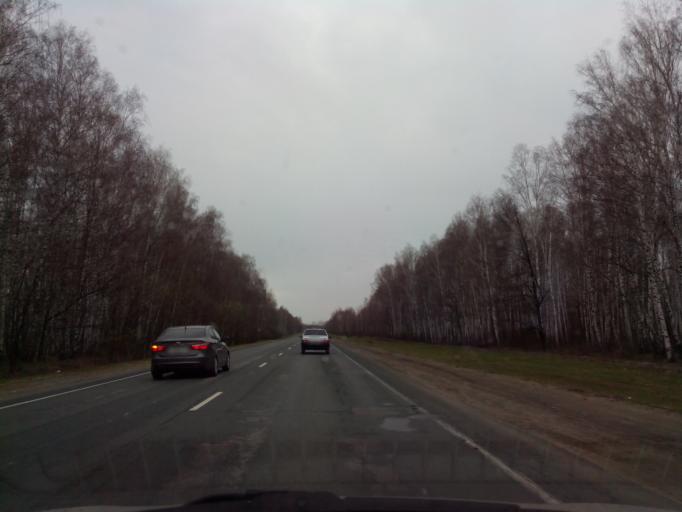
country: RU
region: Tambov
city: Michurinsk
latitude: 53.0741
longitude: 40.4245
